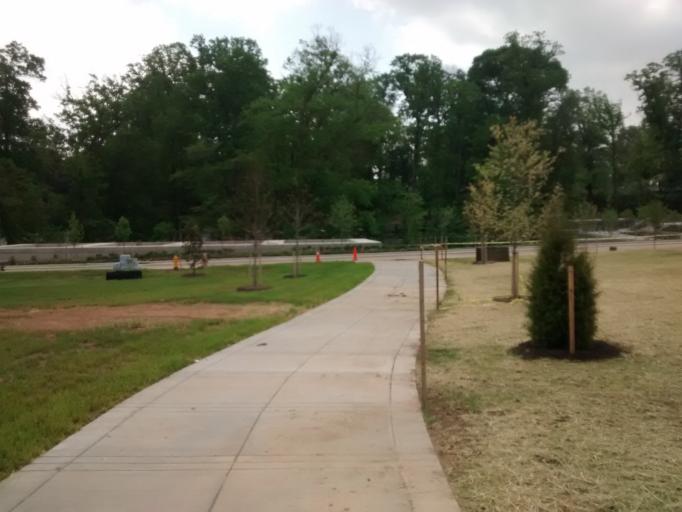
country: US
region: Virginia
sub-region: Arlington County
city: Arlington
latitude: 38.8825
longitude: -77.0781
